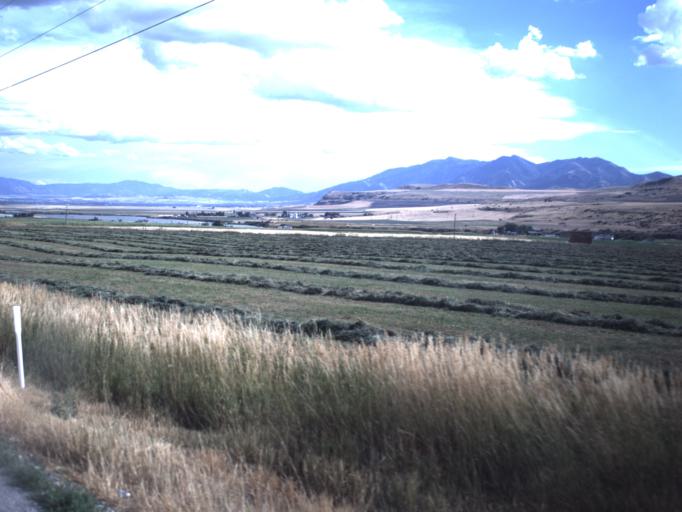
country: US
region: Utah
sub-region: Cache County
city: Benson
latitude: 41.8691
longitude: -112.0119
